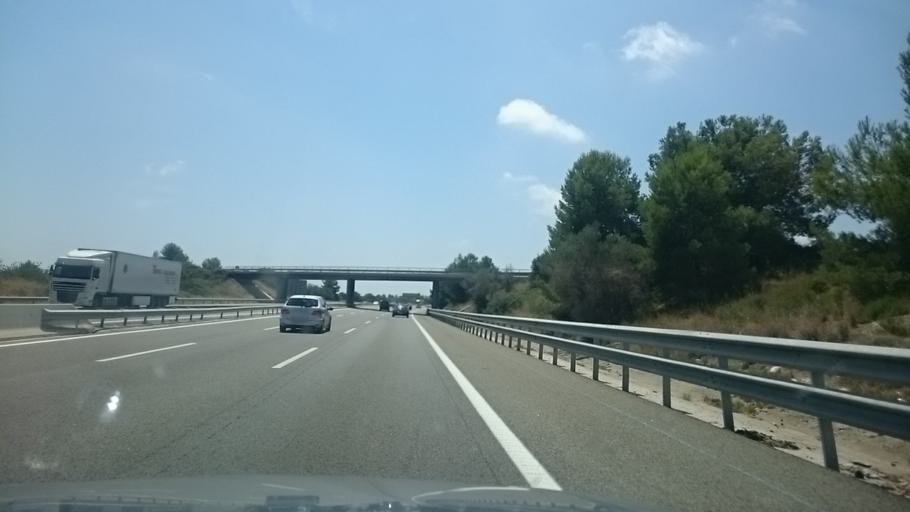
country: ES
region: Catalonia
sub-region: Provincia de Tarragona
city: El Vendrell
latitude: 41.2373
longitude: 1.5274
